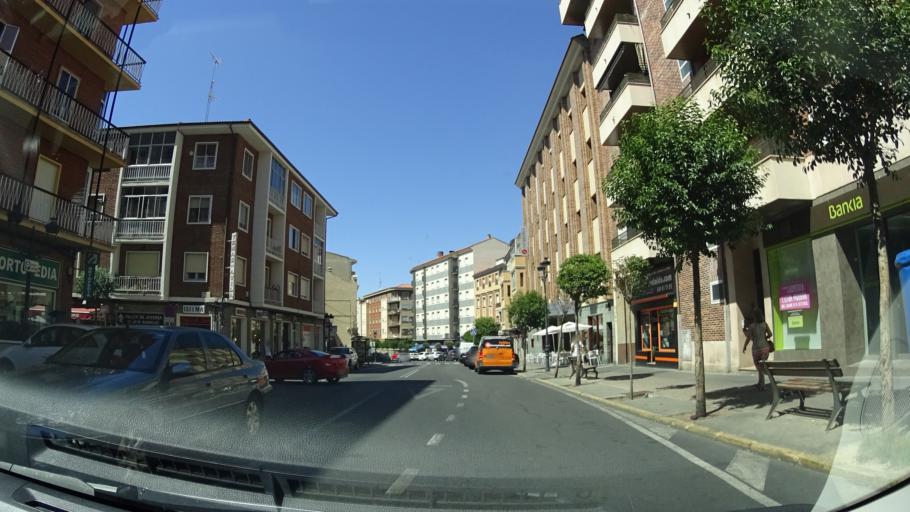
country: ES
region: Castille and Leon
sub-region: Provincia de Avila
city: Avila
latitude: 40.6571
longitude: -4.6852
